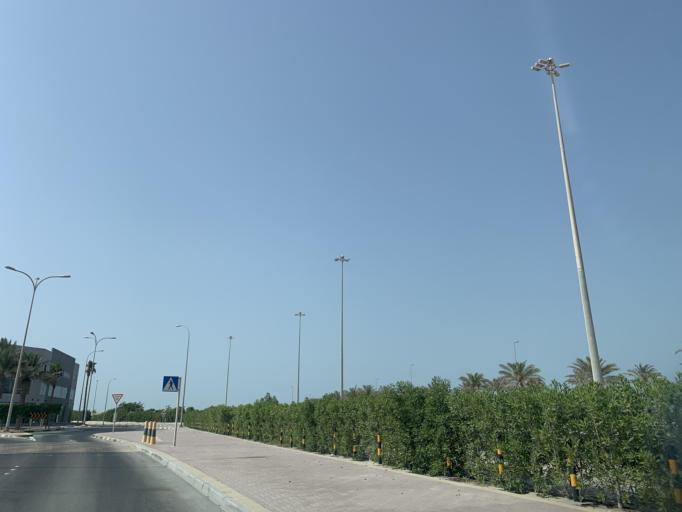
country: BH
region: Muharraq
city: Al Muharraq
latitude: 26.3062
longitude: 50.6393
